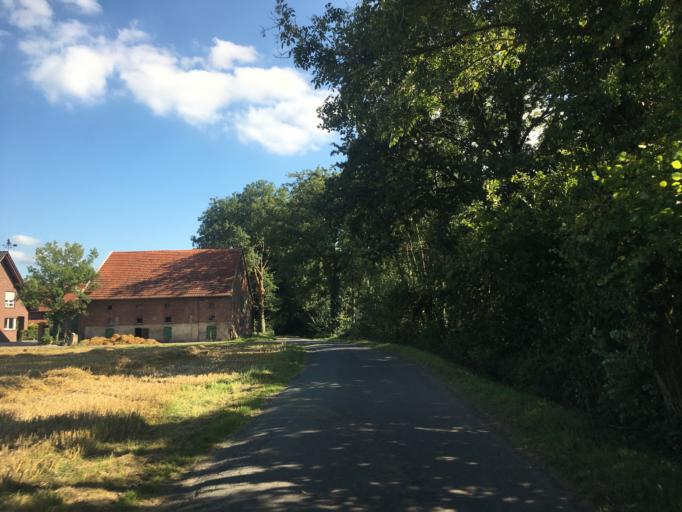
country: DE
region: North Rhine-Westphalia
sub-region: Regierungsbezirk Munster
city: Muenster
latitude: 51.9805
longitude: 7.5852
